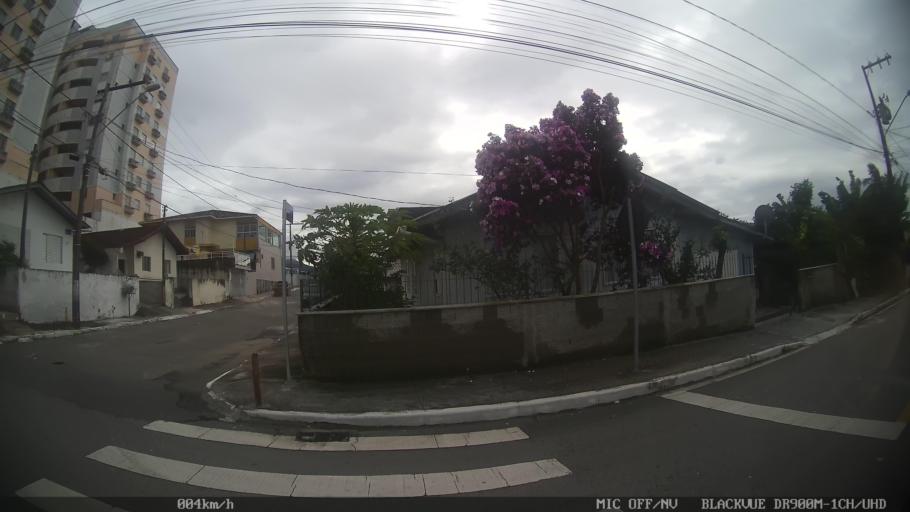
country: BR
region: Santa Catarina
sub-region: Sao Jose
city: Campinas
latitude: -27.5629
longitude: -48.6341
